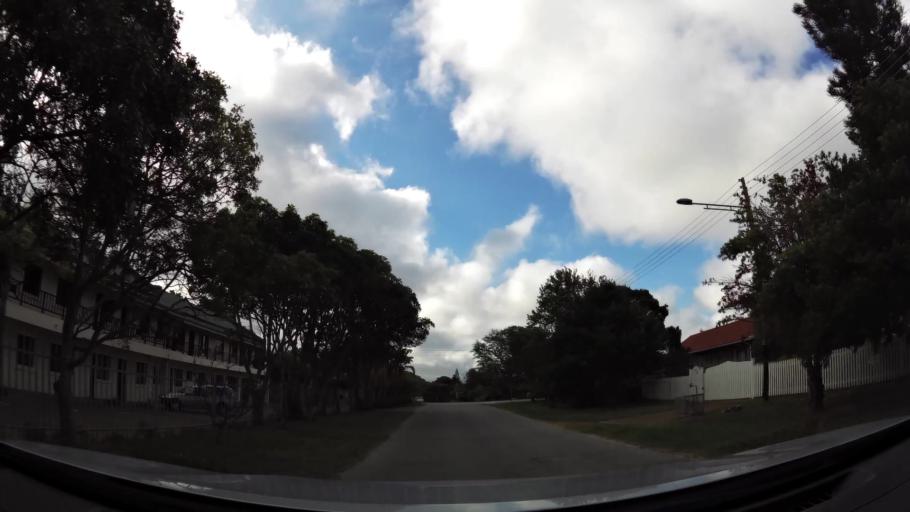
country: ZA
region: Western Cape
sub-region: Eden District Municipality
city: Plettenberg Bay
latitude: -34.0734
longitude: 23.3682
